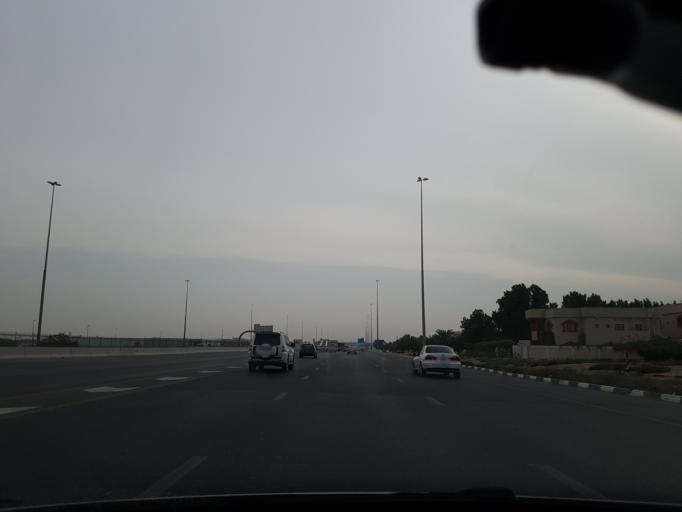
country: AE
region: Ash Shariqah
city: Sharjah
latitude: 25.3547
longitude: 55.4794
